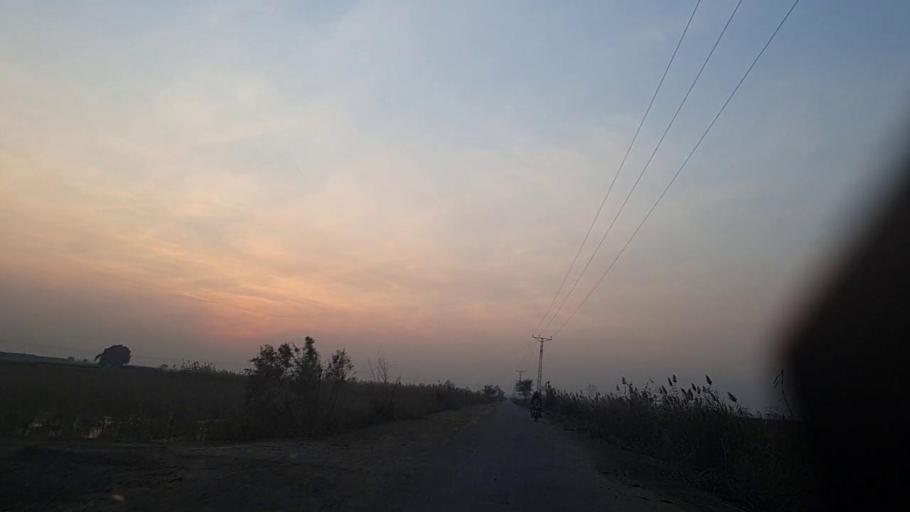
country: PK
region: Sindh
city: Sakrand
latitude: 26.0991
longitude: 68.3334
